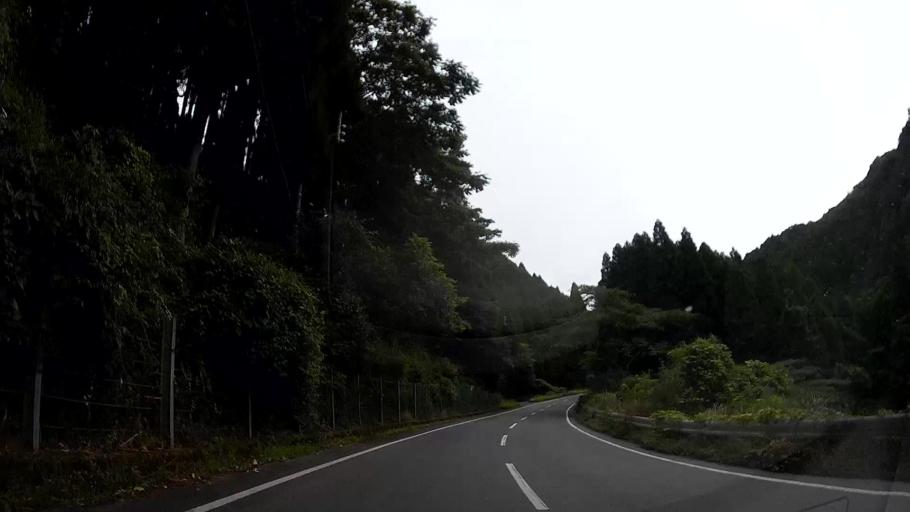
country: JP
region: Kumamoto
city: Kikuchi
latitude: 33.0438
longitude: 130.8944
